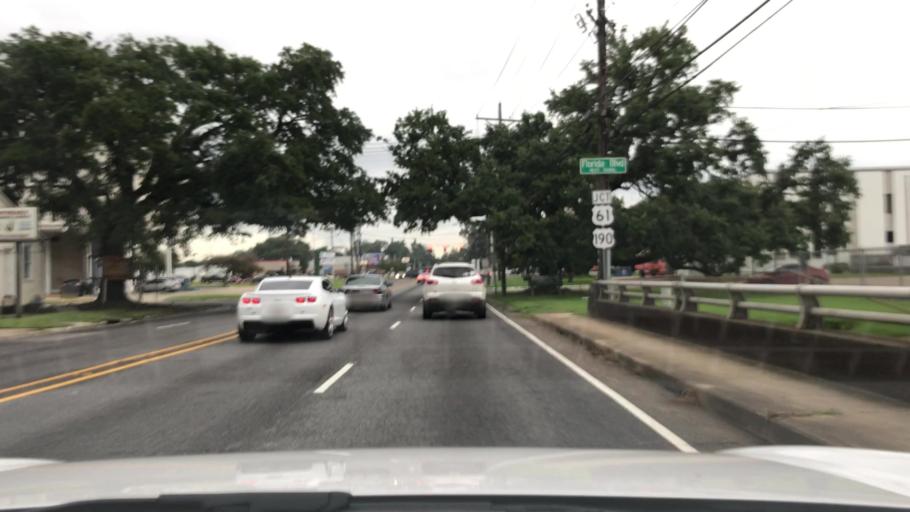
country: US
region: Louisiana
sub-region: East Baton Rouge Parish
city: Baton Rouge
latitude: 30.4492
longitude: -91.1389
